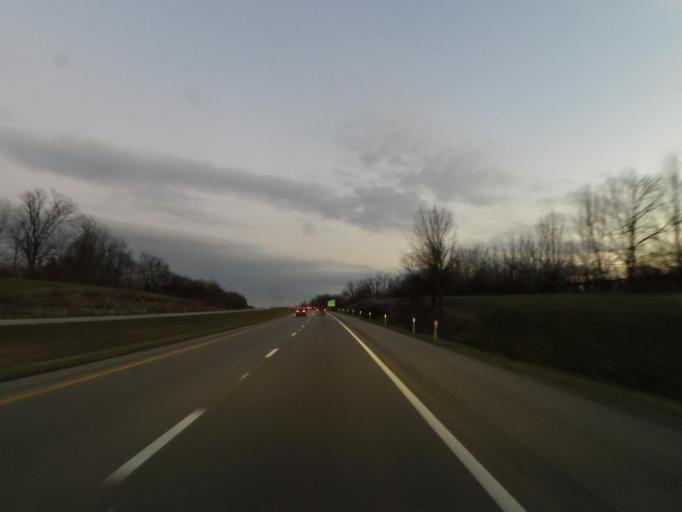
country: US
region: Kentucky
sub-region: Scott County
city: Georgetown
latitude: 38.1312
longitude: -84.5591
